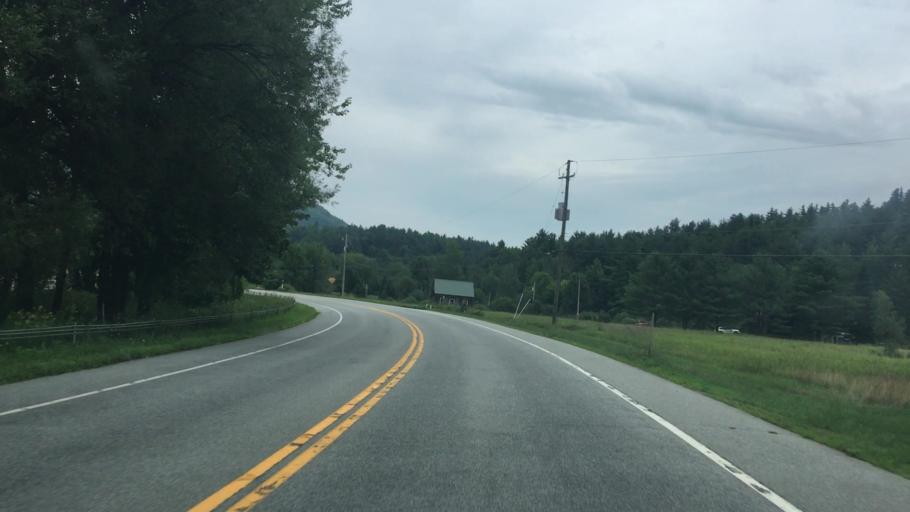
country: US
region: New York
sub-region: Essex County
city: Lake Placid
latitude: 44.3278
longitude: -73.7736
